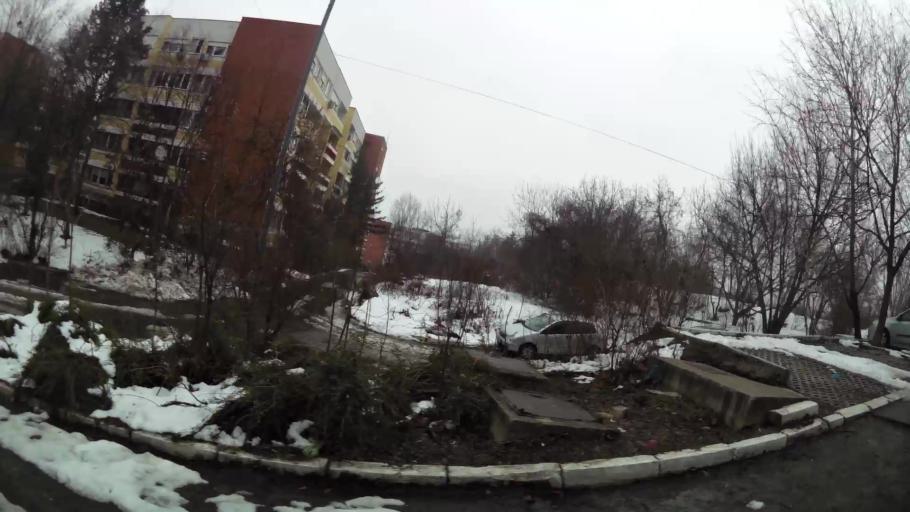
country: RS
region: Central Serbia
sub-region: Belgrade
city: Vozdovac
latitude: 44.7505
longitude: 20.4992
